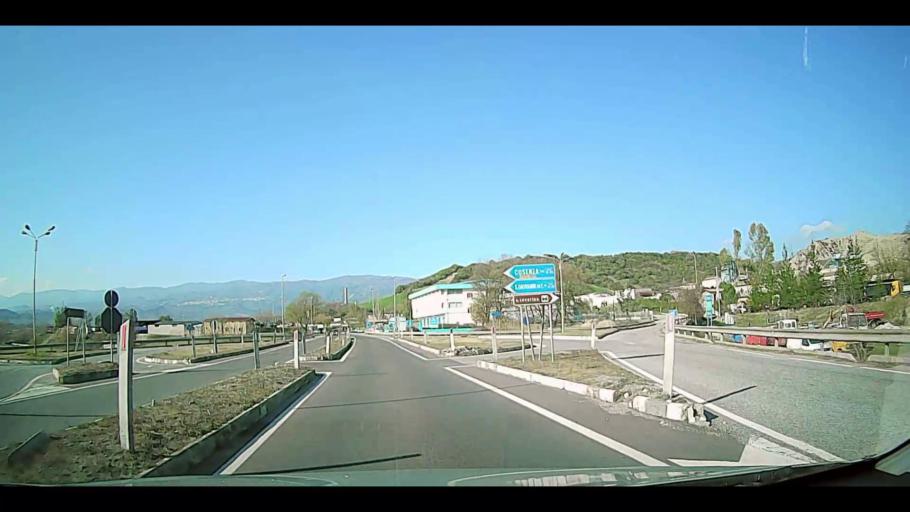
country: IT
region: Calabria
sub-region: Provincia di Crotone
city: Belvedere Spinello
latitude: 39.1887
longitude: 16.8479
